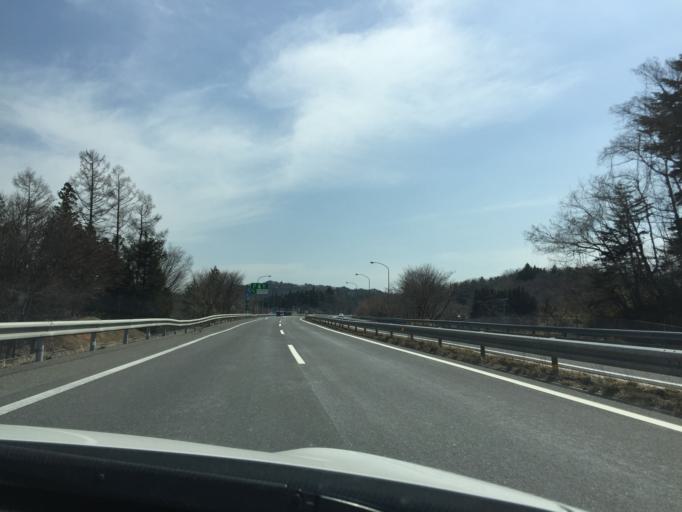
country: JP
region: Fukushima
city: Funehikimachi-funehiki
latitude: 37.3905
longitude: 140.5922
